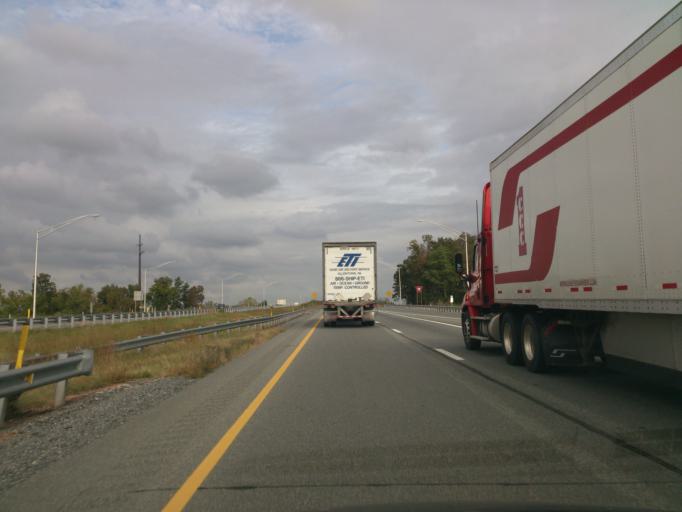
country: US
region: Pennsylvania
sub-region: Lancaster County
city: Swartzville
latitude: 40.2173
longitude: -76.0878
